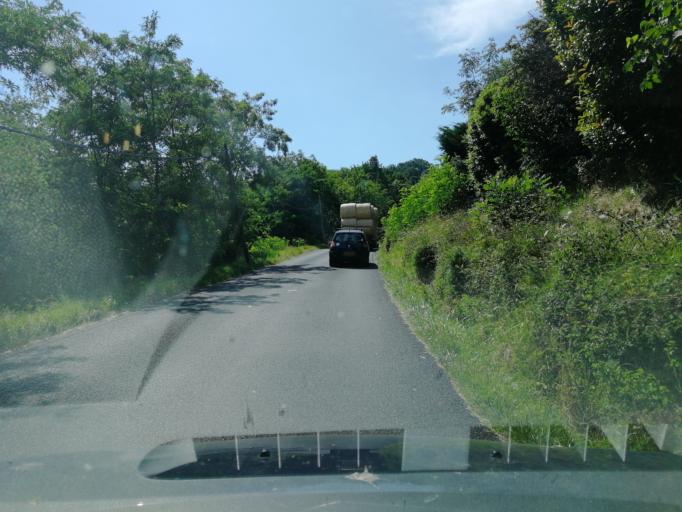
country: FR
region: Rhone-Alpes
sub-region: Departement du Rhone
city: Mornant
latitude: 45.6340
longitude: 4.6367
